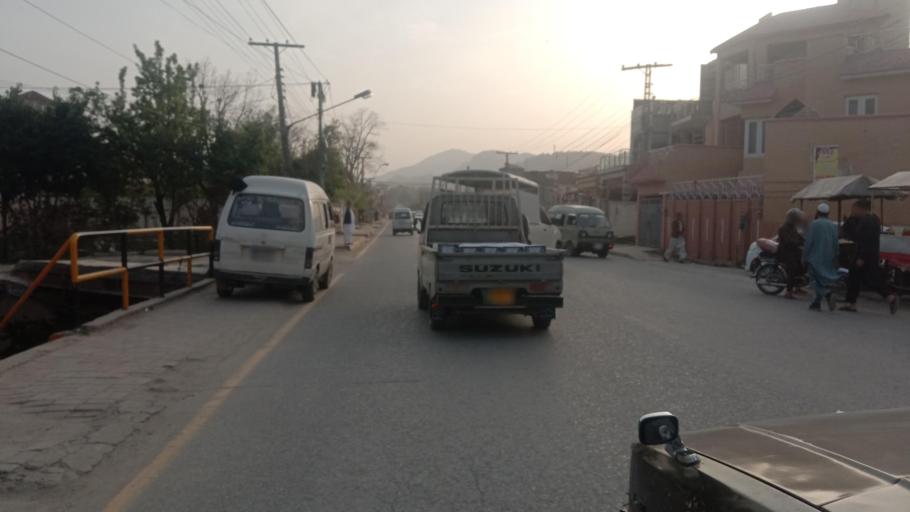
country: PK
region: Khyber Pakhtunkhwa
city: Abbottabad
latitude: 34.1706
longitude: 73.2330
